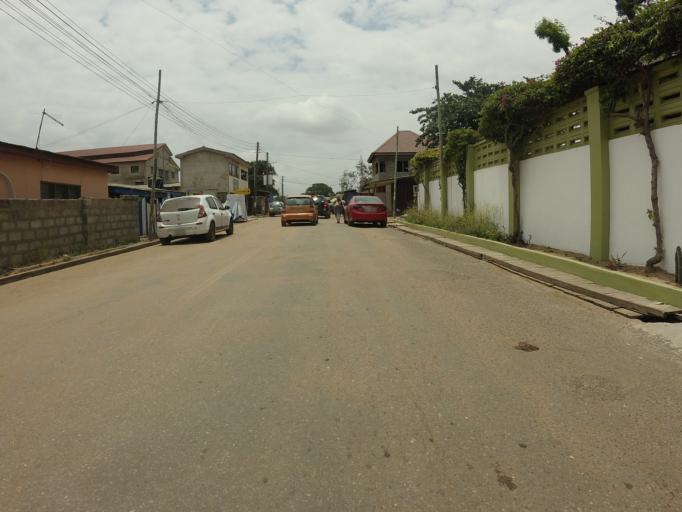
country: GH
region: Greater Accra
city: Nungua
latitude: 5.6024
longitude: -0.0851
